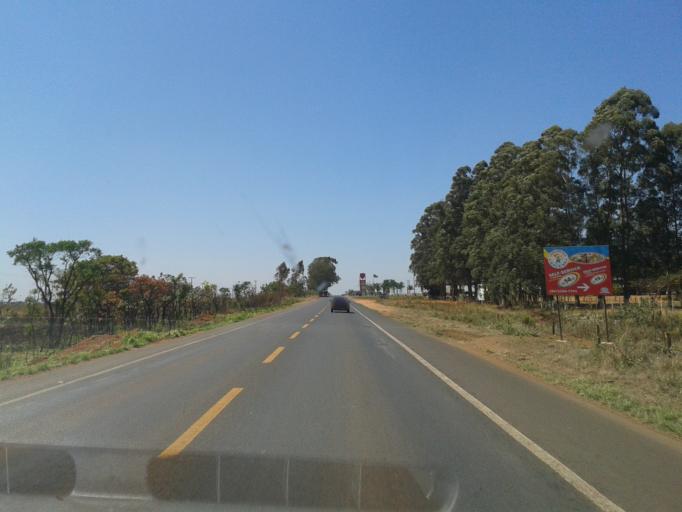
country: BR
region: Minas Gerais
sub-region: Uberaba
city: Uberaba
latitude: -19.3125
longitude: -47.5743
